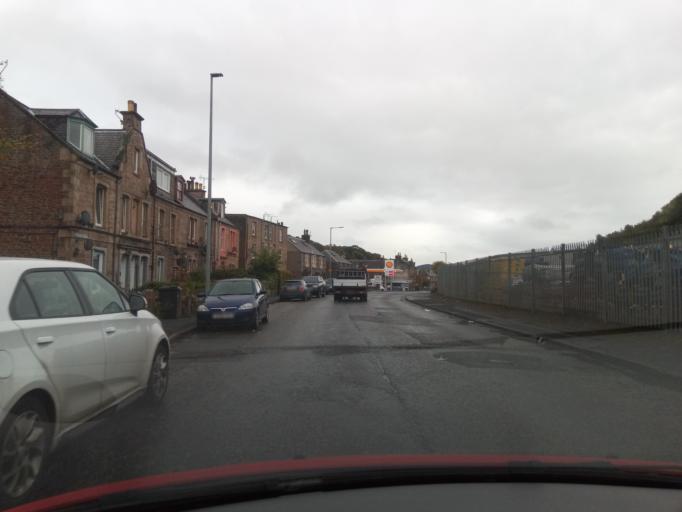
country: GB
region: Scotland
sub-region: The Scottish Borders
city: Galashiels
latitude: 55.6219
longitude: -2.8189
